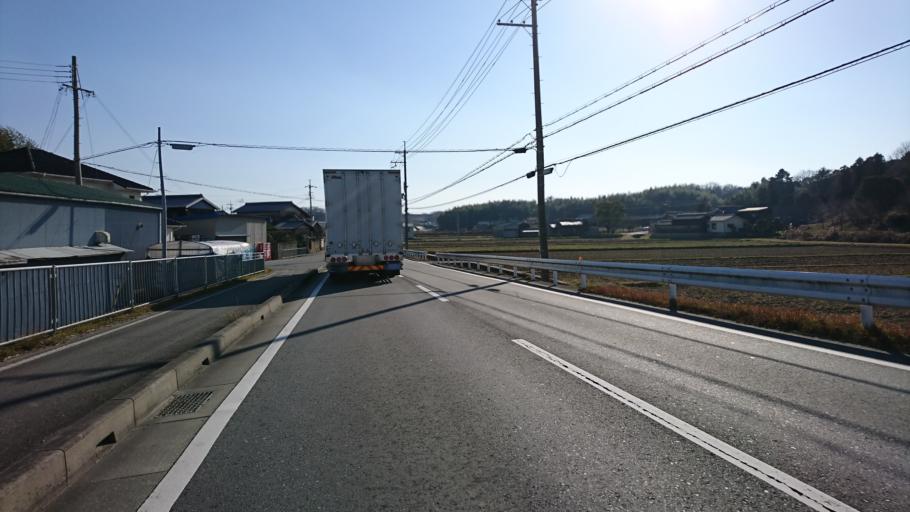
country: JP
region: Hyogo
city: Ono
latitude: 34.7891
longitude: 134.9010
